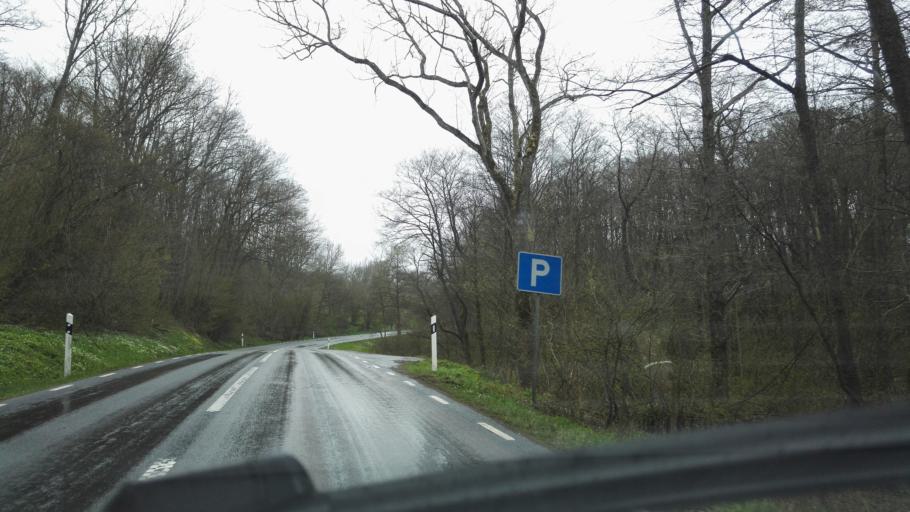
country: SE
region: Skane
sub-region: Simrishamns Kommun
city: Kivik
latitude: 55.6547
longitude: 14.2189
